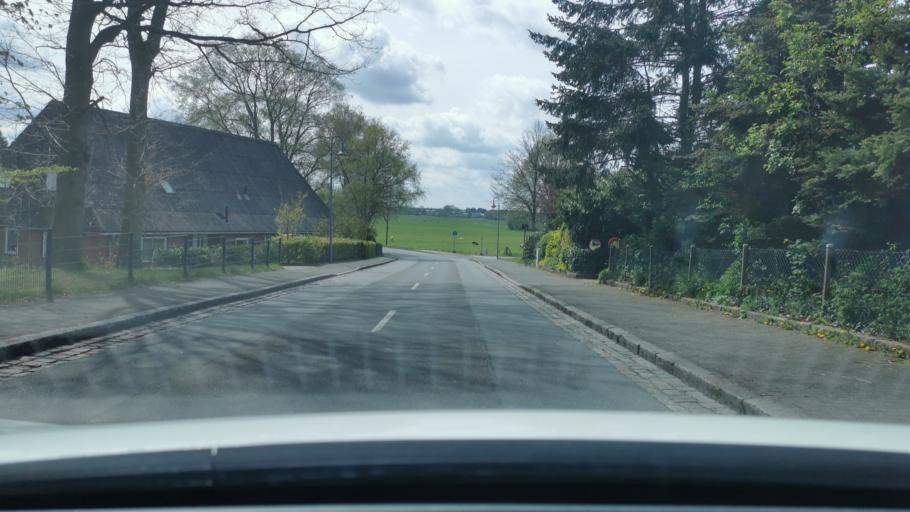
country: DE
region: Schleswig-Holstein
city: Hamdorf
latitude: 54.2191
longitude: 9.5187
